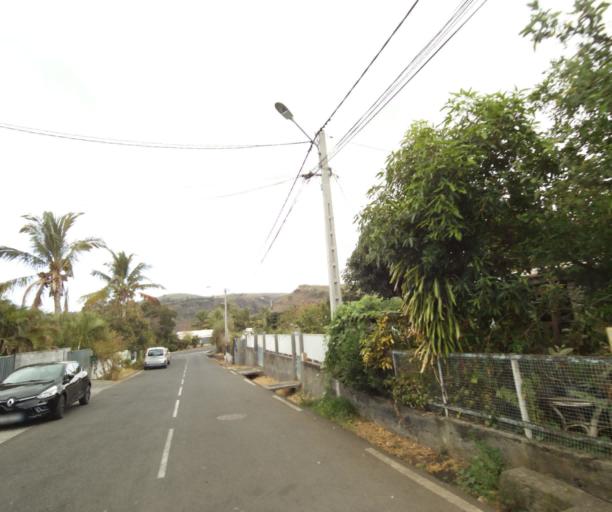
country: RE
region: Reunion
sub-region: Reunion
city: Saint-Paul
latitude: -21.0542
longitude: 55.2334
